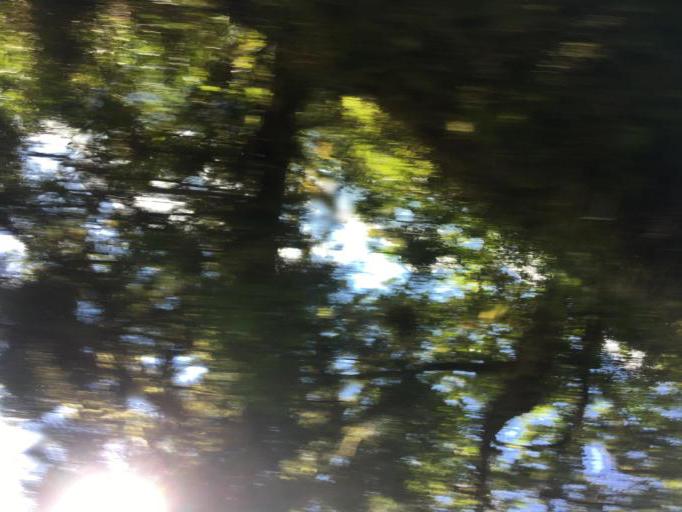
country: TW
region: Taiwan
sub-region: Yilan
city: Yilan
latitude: 24.5064
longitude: 121.5691
